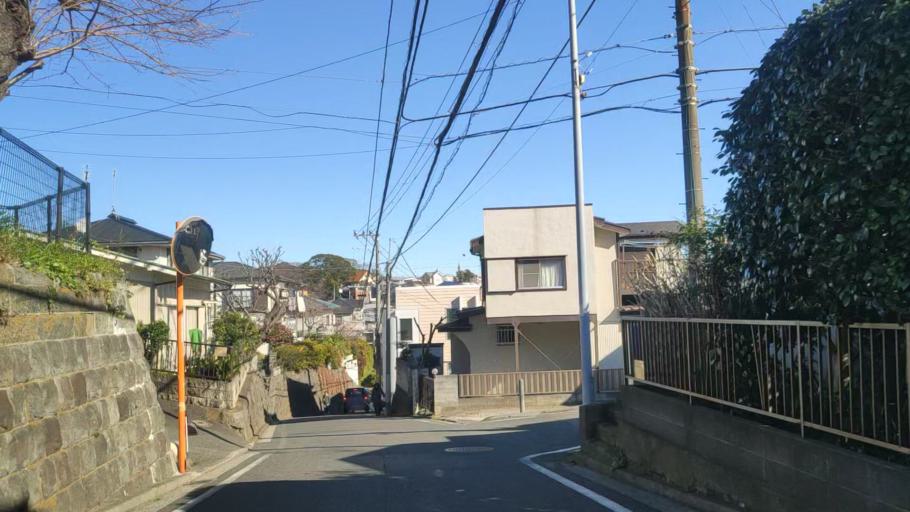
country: JP
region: Kanagawa
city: Yokohama
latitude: 35.4320
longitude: 139.6462
